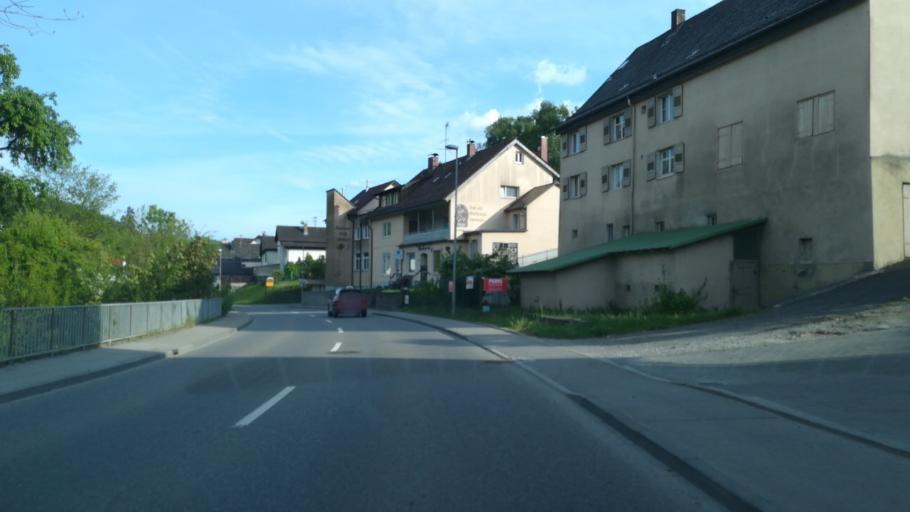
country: DE
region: Baden-Wuerttemberg
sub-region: Freiburg Region
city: Stockach
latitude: 47.8732
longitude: 9.0007
